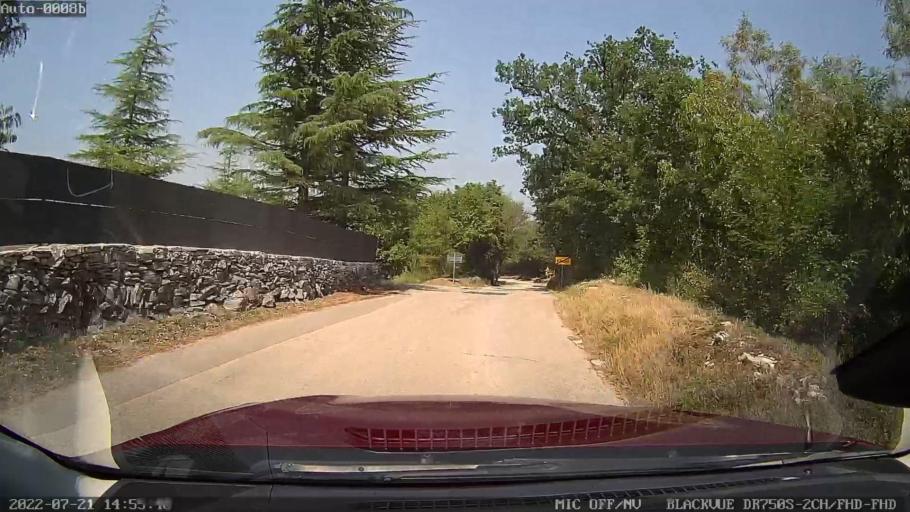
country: HR
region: Istarska
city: Pazin
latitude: 45.1976
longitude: 13.9448
